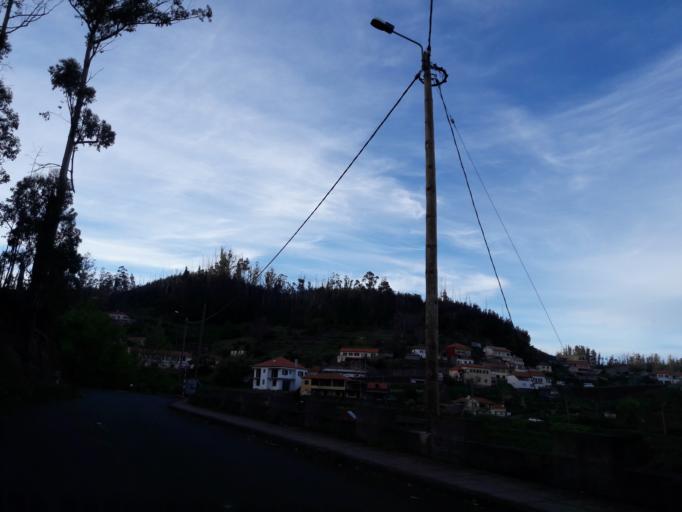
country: PT
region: Madeira
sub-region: Santa Cruz
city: Camacha
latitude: 32.6899
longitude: -16.8655
